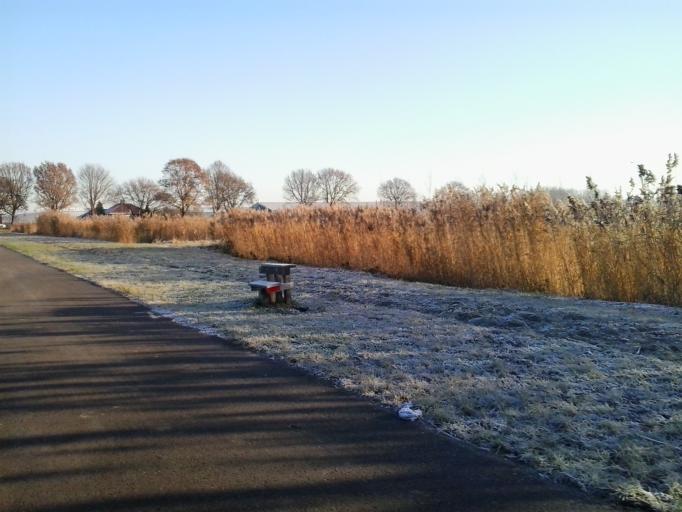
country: NL
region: South Holland
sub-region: Gemeente Lansingerland
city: Bergschenhoek
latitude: 51.9785
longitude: 4.5195
